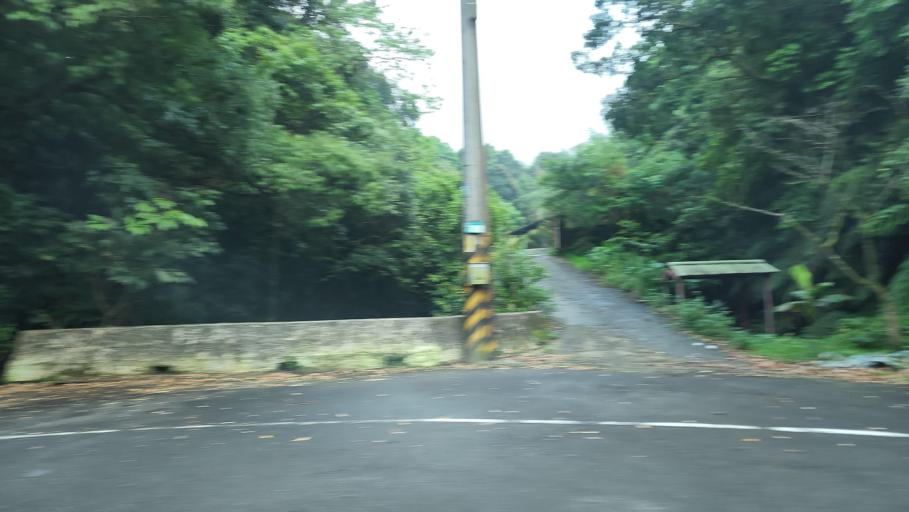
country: TW
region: Taipei
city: Taipei
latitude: 25.1456
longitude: 121.6107
